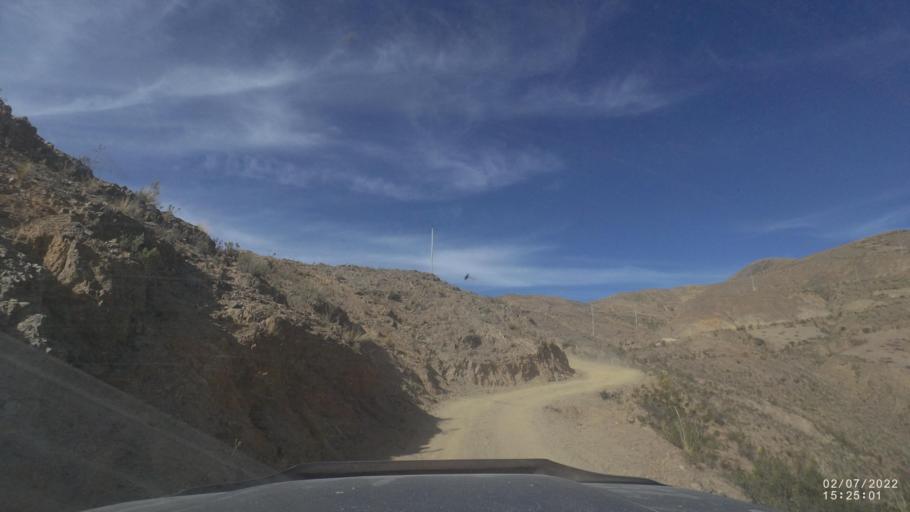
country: BO
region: Cochabamba
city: Irpa Irpa
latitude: -17.8752
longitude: -66.4173
